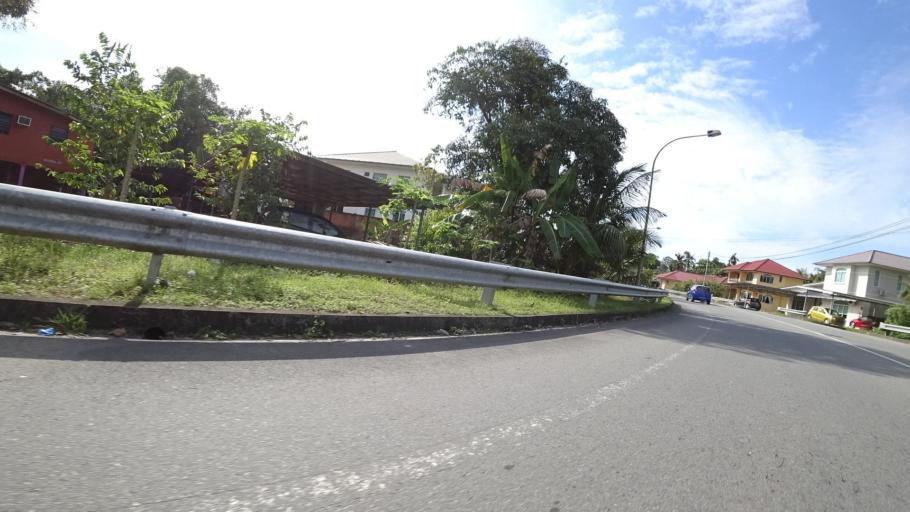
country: BN
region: Brunei and Muara
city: Bandar Seri Begawan
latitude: 4.8725
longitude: 114.8078
